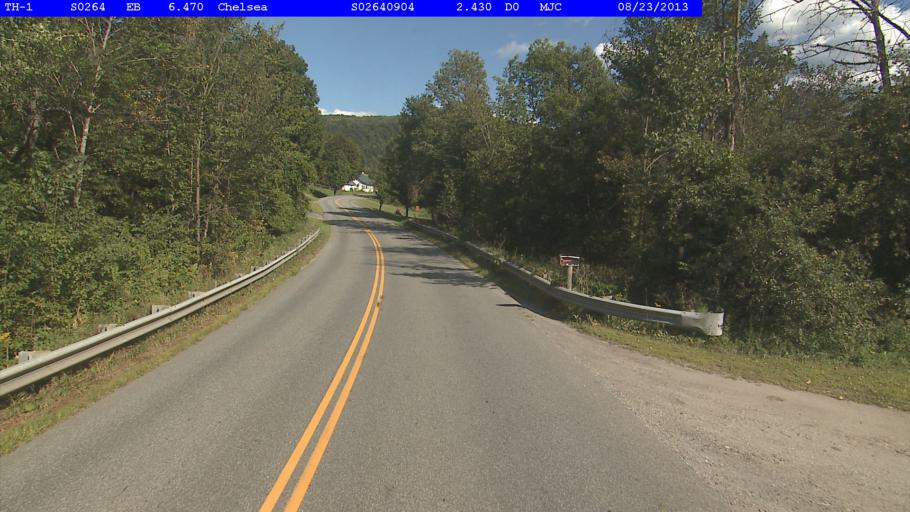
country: US
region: Vermont
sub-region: Orange County
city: Chelsea
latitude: 43.9635
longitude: -72.4726
